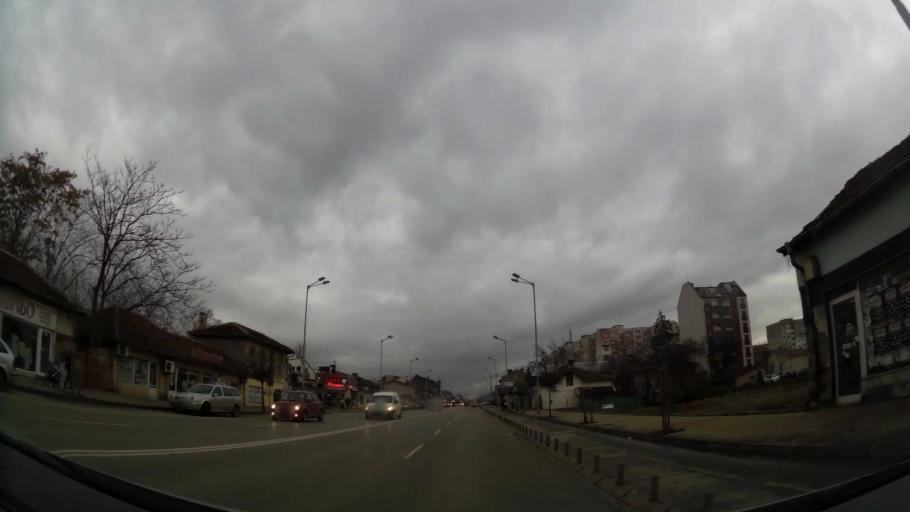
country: BG
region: Sofia-Capital
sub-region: Stolichna Obshtina
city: Sofia
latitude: 42.7290
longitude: 23.2997
